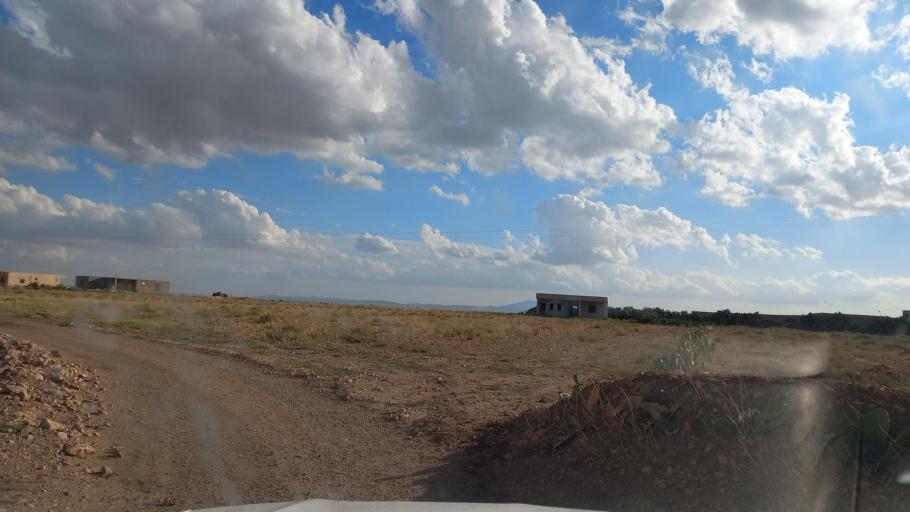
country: TN
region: Al Qasrayn
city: Sbiba
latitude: 35.3841
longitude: 9.0692
